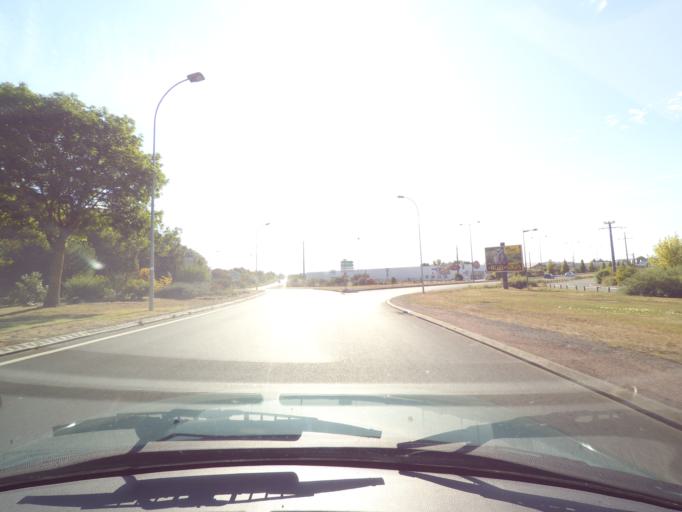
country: FR
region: Poitou-Charentes
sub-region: Departement de la Vienne
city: Migne-Auxances
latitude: 46.6167
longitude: 0.3133
